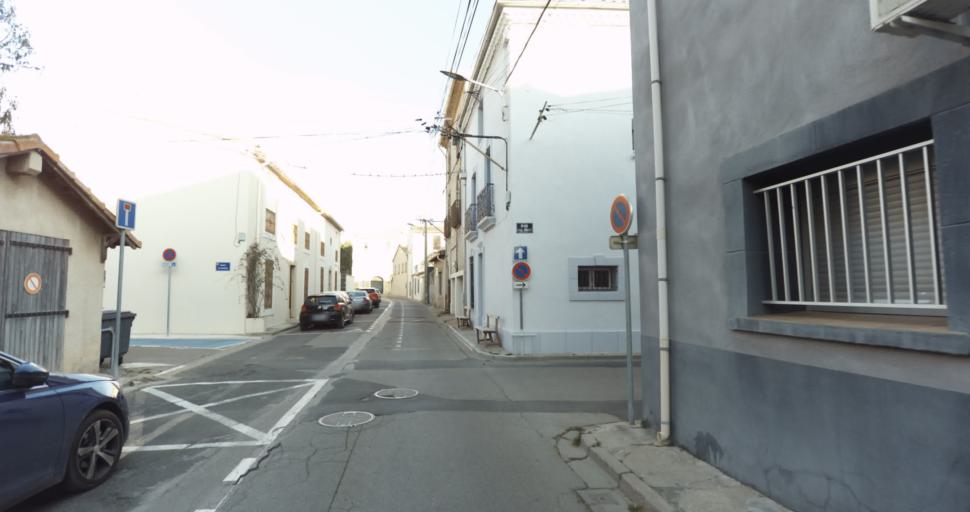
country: FR
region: Languedoc-Roussillon
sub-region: Departement de l'Herault
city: Marseillan
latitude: 43.3563
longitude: 3.5257
